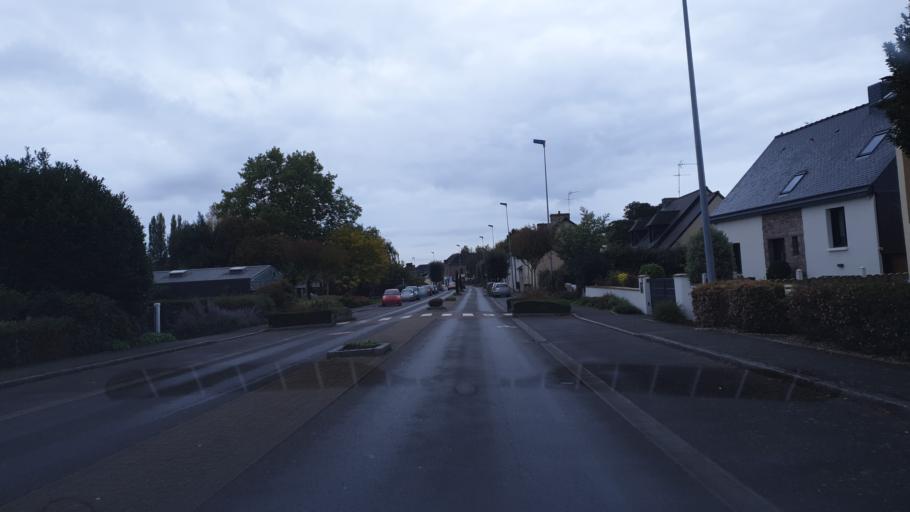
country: FR
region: Brittany
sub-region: Departement d'Ille-et-Vilaine
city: Chartres-de-Bretagne
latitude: 48.0449
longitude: -1.7110
